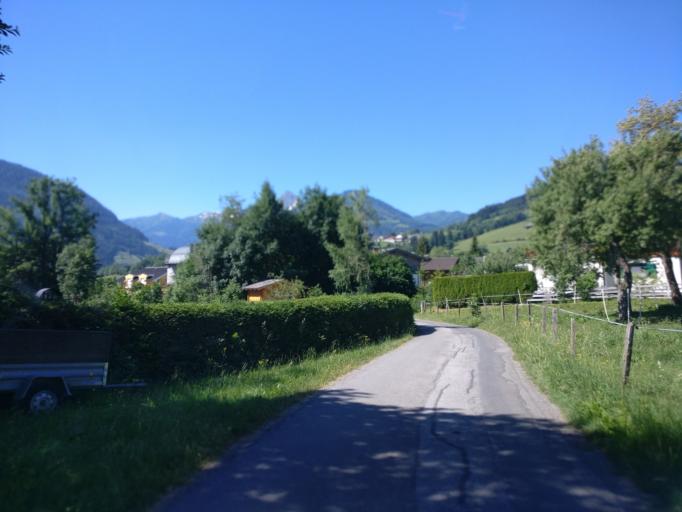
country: AT
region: Salzburg
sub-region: Politischer Bezirk Sankt Johann im Pongau
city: Goldegg
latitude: 47.3177
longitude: 13.0876
